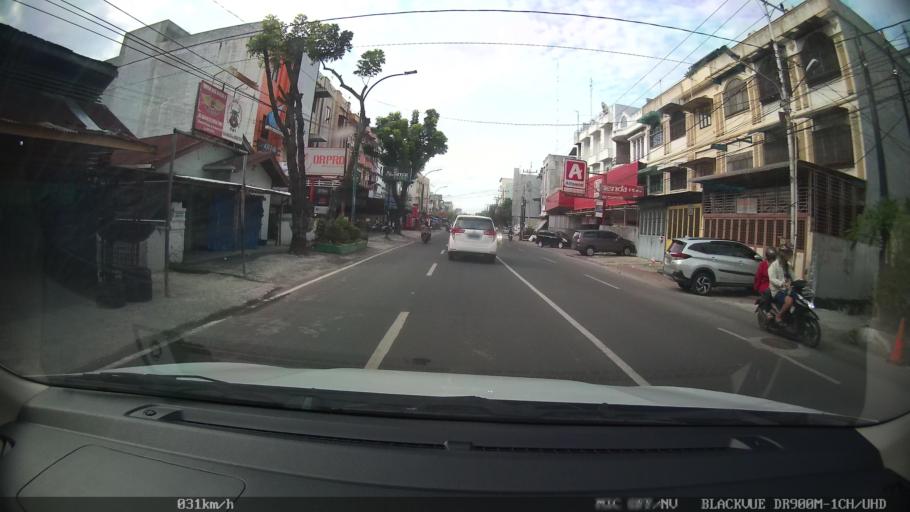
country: ID
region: North Sumatra
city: Medan
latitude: 3.6044
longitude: 98.6768
